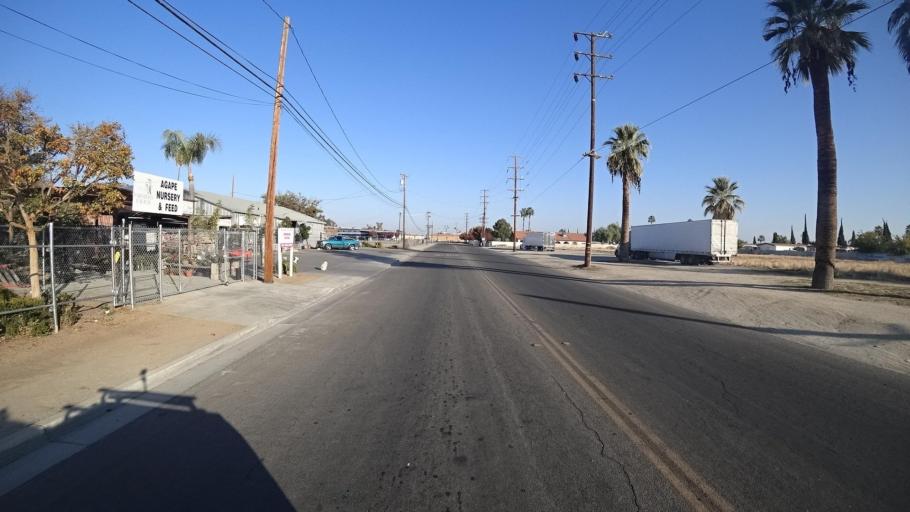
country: US
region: California
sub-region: Kern County
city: Delano
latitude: 35.7833
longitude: -119.2498
